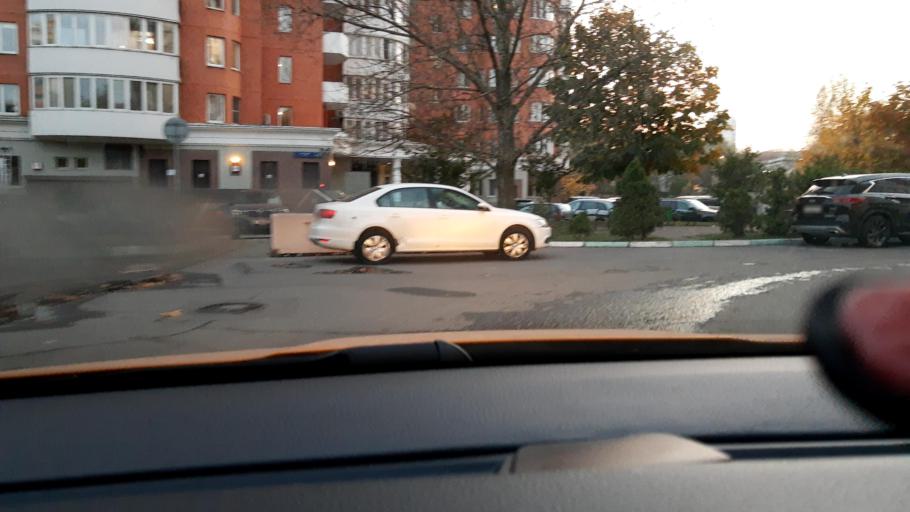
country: RU
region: Moskovskaya
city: Bol'shaya Setun'
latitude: 55.7230
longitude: 37.4123
